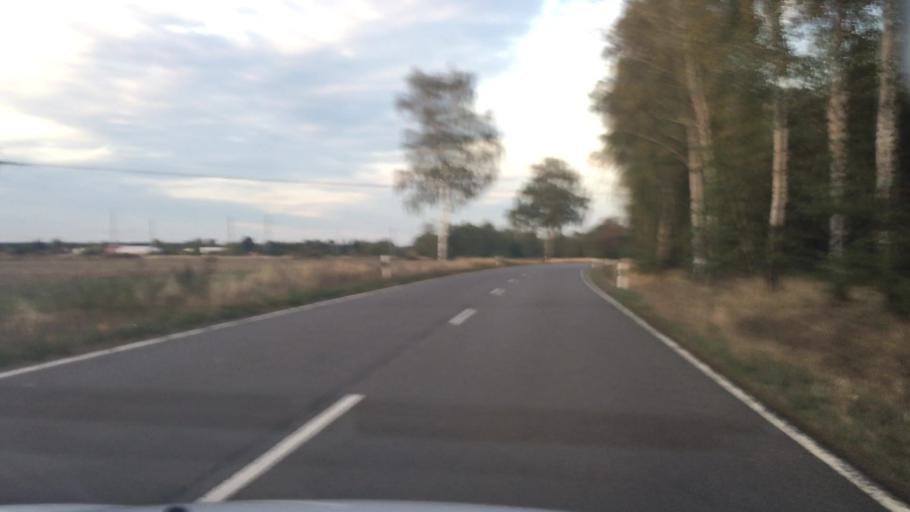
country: DE
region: Brandenburg
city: Grossraschen
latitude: 51.5736
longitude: 14.0834
